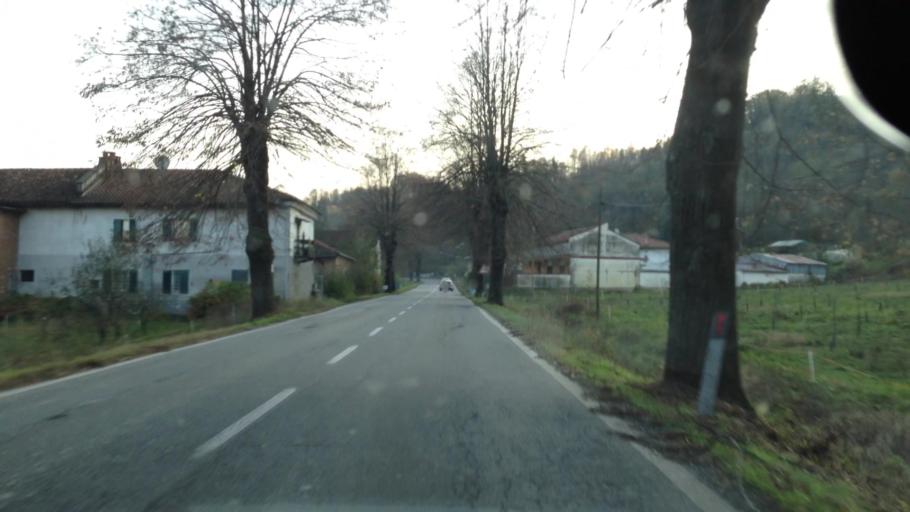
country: IT
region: Piedmont
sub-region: Provincia di Torino
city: Cavagnolo
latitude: 45.1377
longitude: 8.0552
